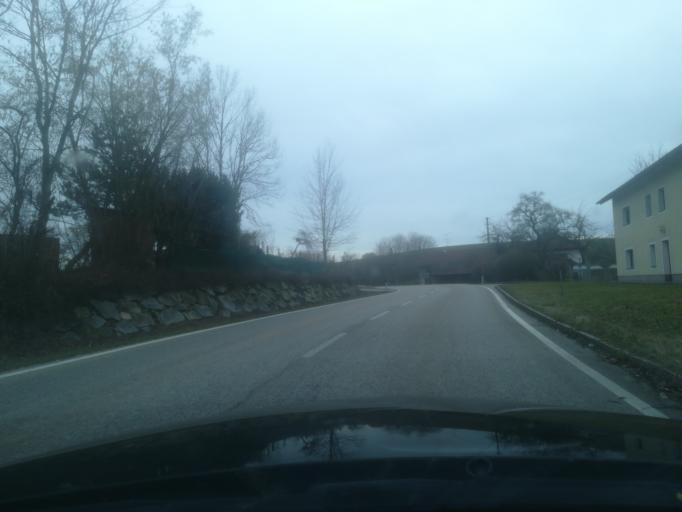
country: AT
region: Upper Austria
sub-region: Wels-Land
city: Neukirchen bei Lambach
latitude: 48.1055
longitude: 13.8258
